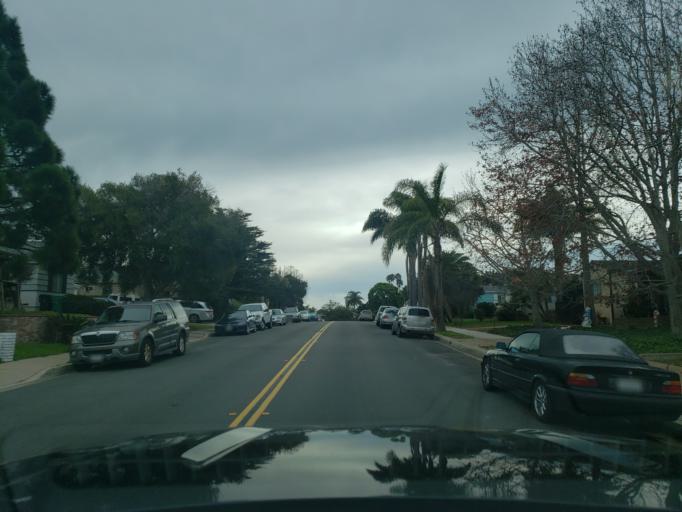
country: US
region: California
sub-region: San Diego County
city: Coronado
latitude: 32.7330
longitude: -117.2390
